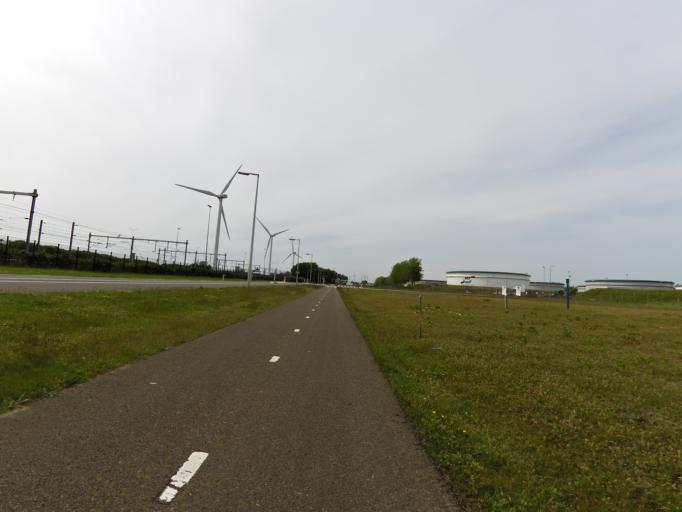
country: NL
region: South Holland
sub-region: Gemeente Brielle
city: Brielle
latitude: 51.9094
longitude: 4.2013
